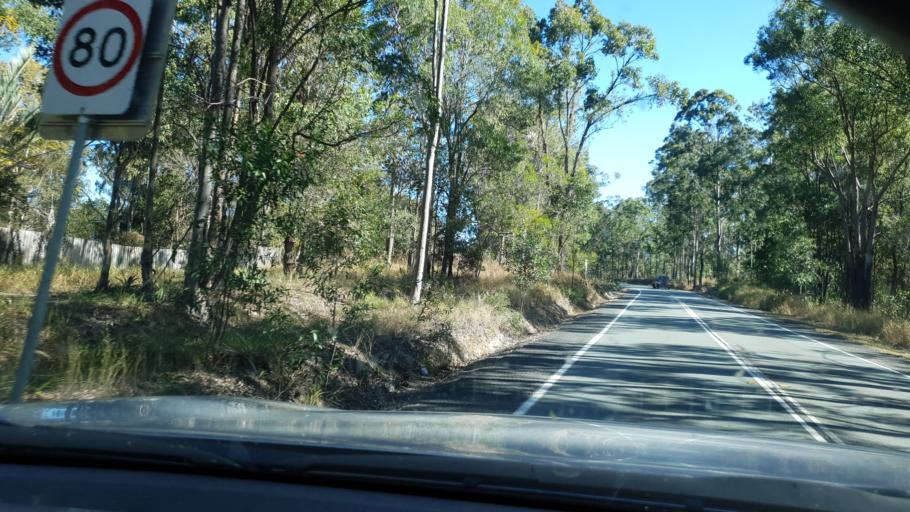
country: AU
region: Queensland
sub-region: Moreton Bay
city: Strathpine
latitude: -27.3289
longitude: 152.9319
